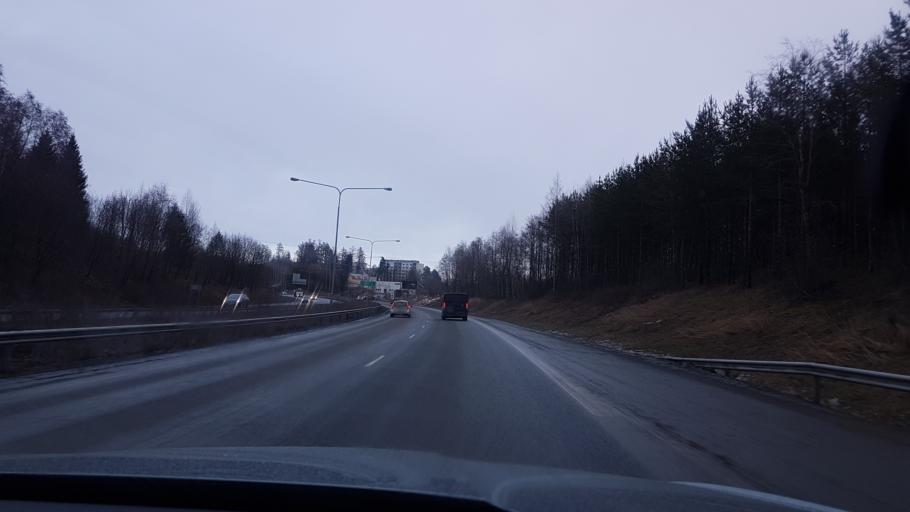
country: FI
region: Pirkanmaa
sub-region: Tampere
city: Tampere
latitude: 61.4699
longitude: 23.8561
